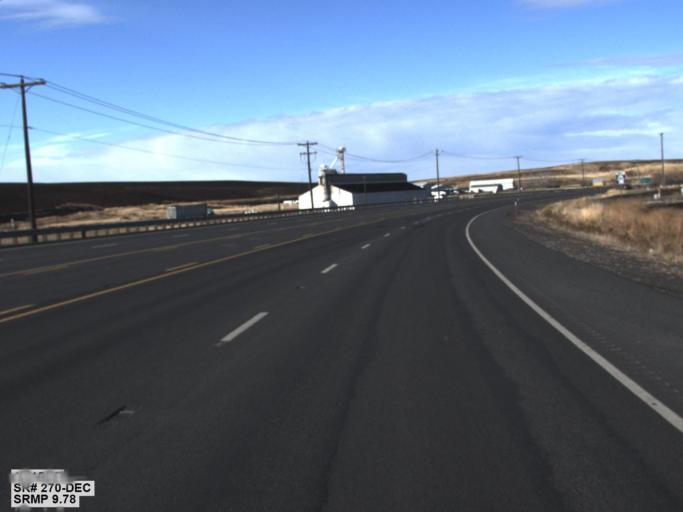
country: US
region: Idaho
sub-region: Latah County
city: Moscow
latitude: 46.7325
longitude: -117.0422
